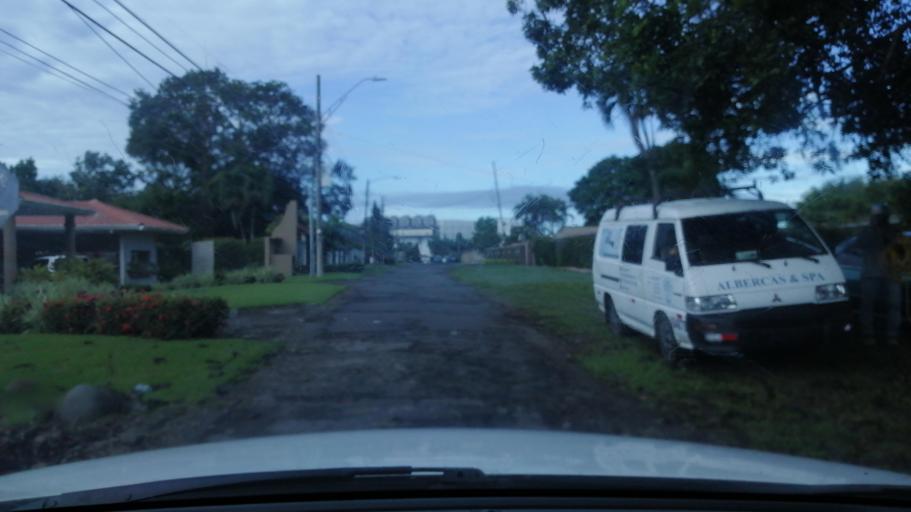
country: PA
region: Chiriqui
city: Mata del Nance
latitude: 8.4484
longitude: -82.4183
